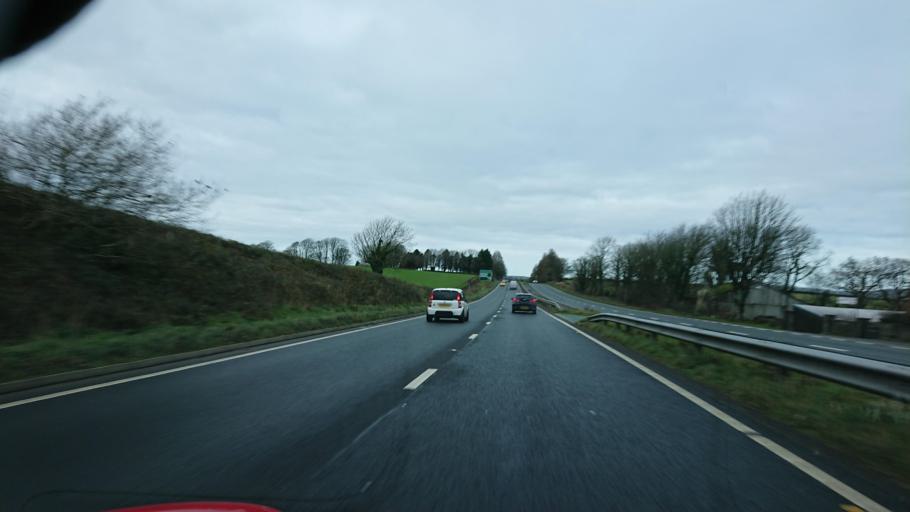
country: GB
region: England
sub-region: Cornwall
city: Liskeard
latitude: 50.4397
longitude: -4.4425
